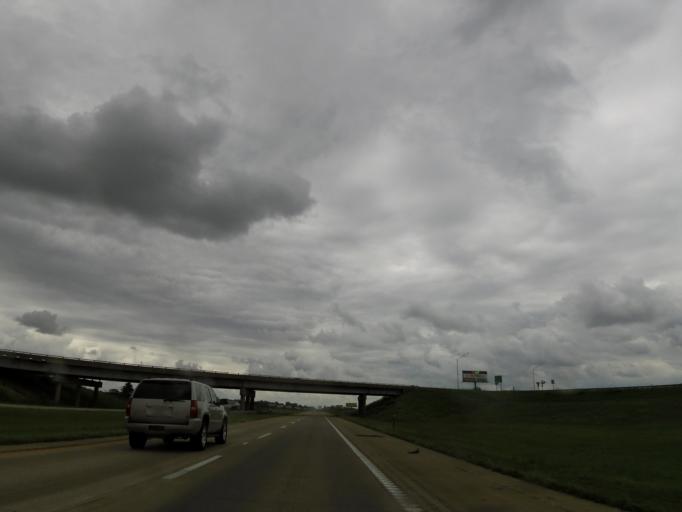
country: US
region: Missouri
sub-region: Mississippi County
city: Charleston
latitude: 36.9201
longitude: -89.3195
